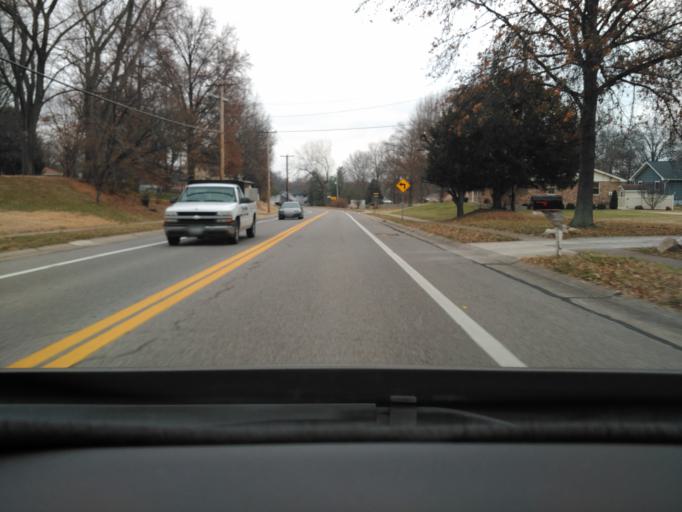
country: US
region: Missouri
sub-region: Saint Louis County
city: Concord
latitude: 38.4983
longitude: -90.3570
